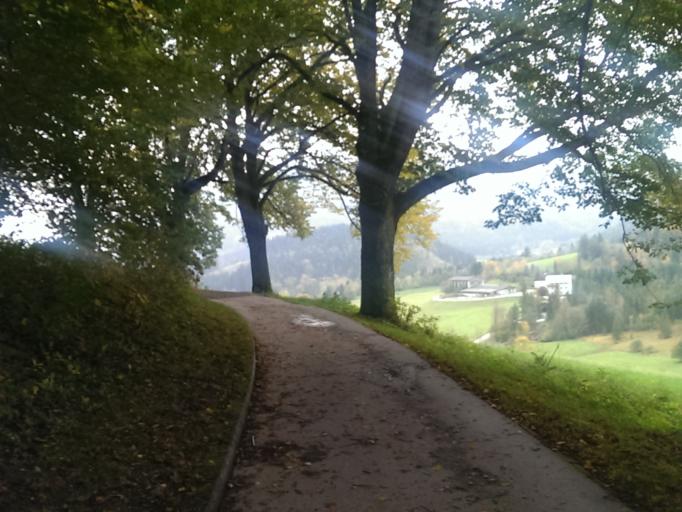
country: AT
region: Styria
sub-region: Politischer Bezirk Bruck-Muerzzuschlag
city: Mariazell
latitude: 47.7771
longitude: 15.3124
